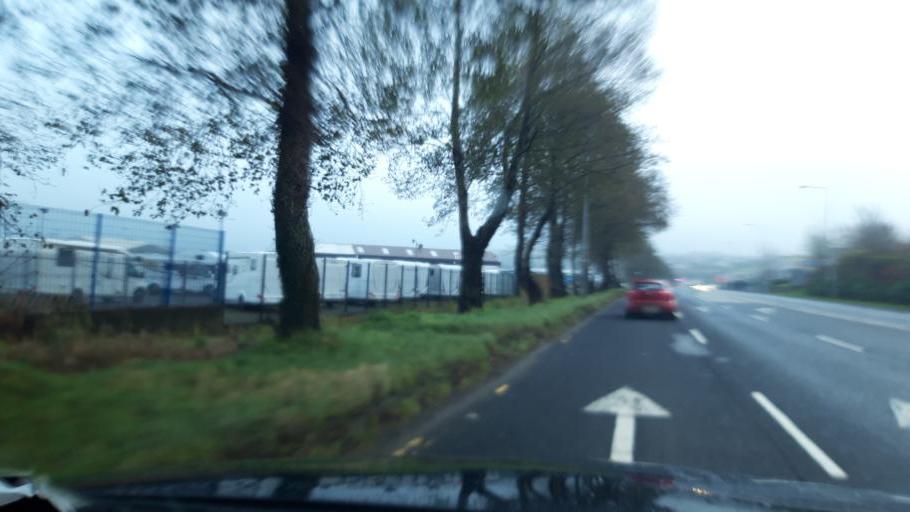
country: IE
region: Ulster
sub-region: County Donegal
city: Letterkenny
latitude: 54.9459
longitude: -7.7044
